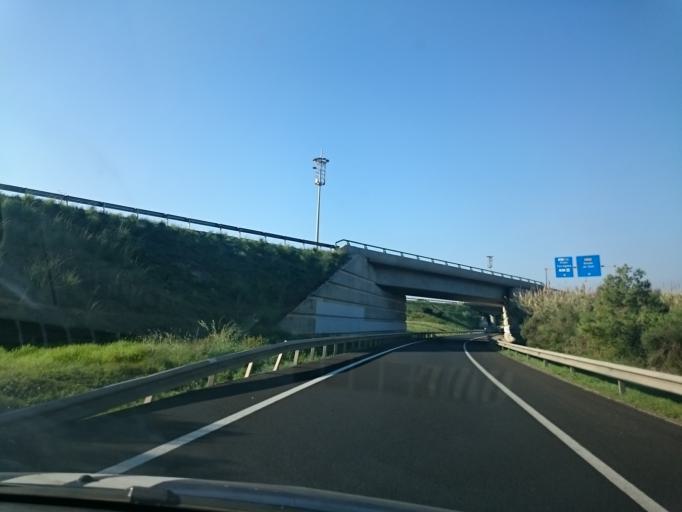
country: ES
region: Catalonia
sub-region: Provincia de Barcelona
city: Cornella de Llobregat
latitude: 41.3436
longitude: 2.0952
